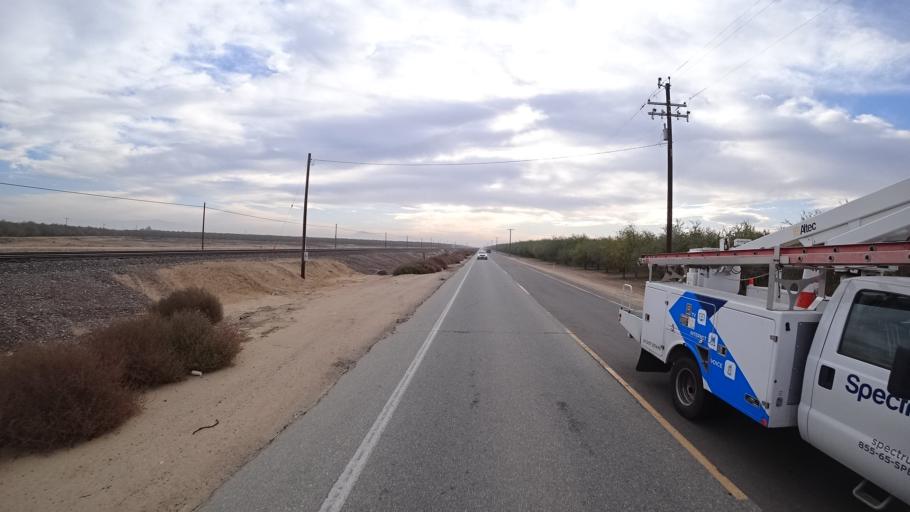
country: US
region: California
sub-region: Kern County
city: Rosedale
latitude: 35.4337
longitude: -119.1894
